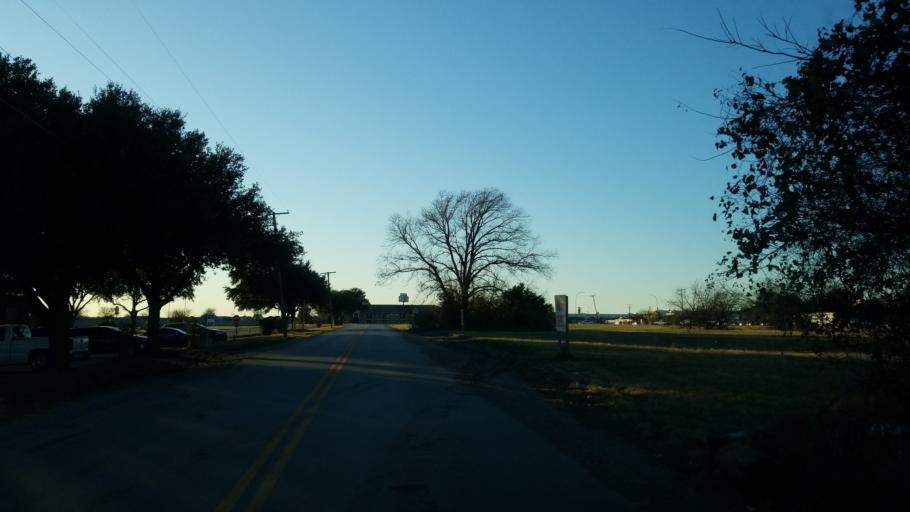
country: US
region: Texas
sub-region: Tarrant County
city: Arlington
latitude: 32.7353
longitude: -97.0572
